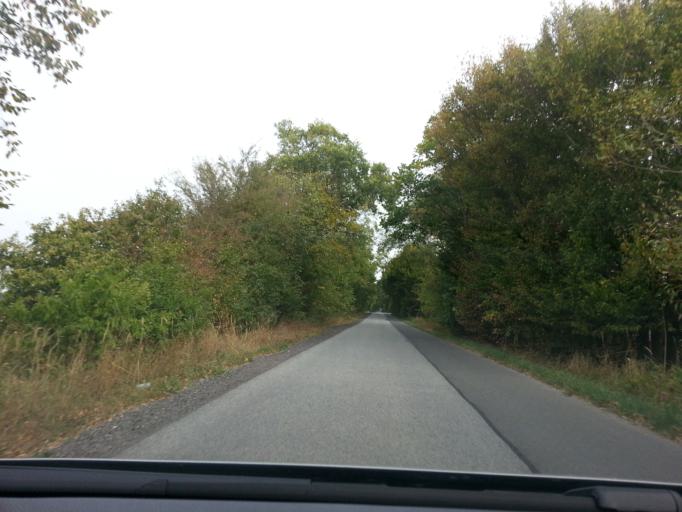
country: DE
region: Mecklenburg-Vorpommern
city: Ferdinandshof
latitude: 53.6504
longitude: 13.9195
